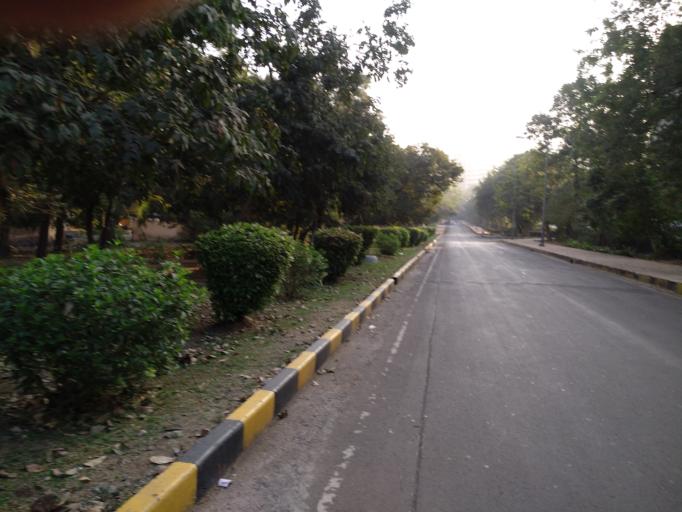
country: IN
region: Maharashtra
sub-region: Mumbai Suburban
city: Mumbai
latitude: 19.0357
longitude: 72.9276
